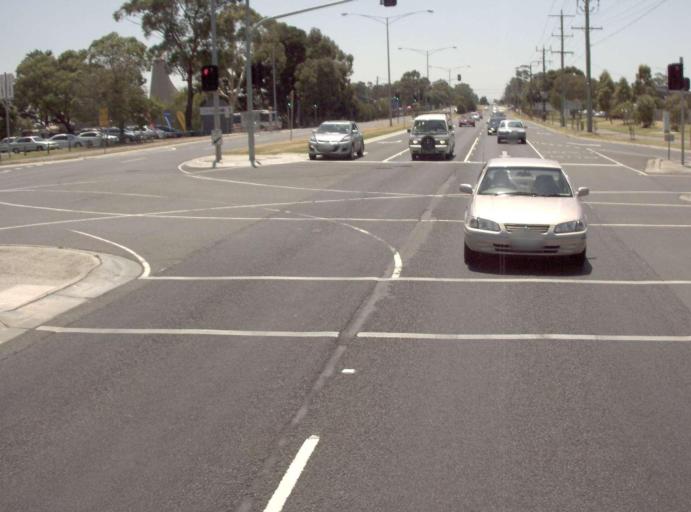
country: AU
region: Victoria
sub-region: Kingston
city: Waterways
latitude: -38.0033
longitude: 145.1423
